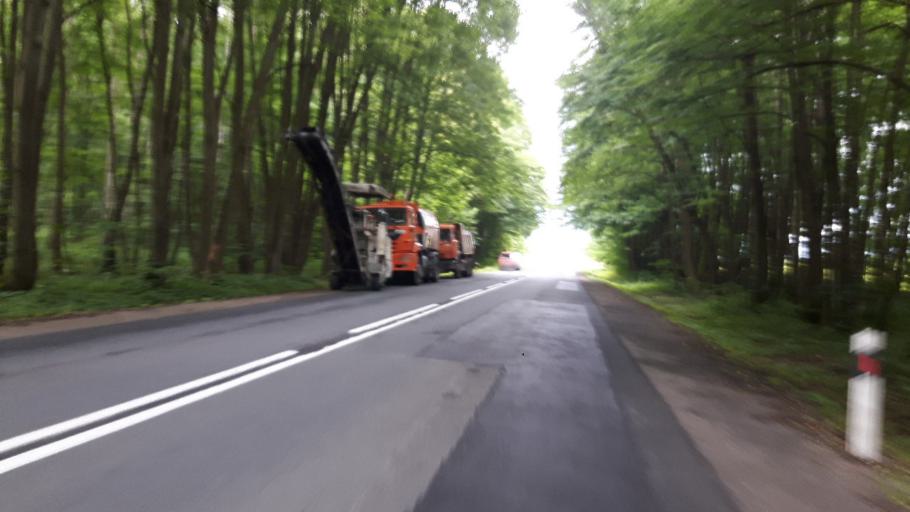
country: RU
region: Kaliningrad
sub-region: Zelenogradskiy Rayon
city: Zelenogradsk
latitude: 54.8356
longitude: 20.4325
